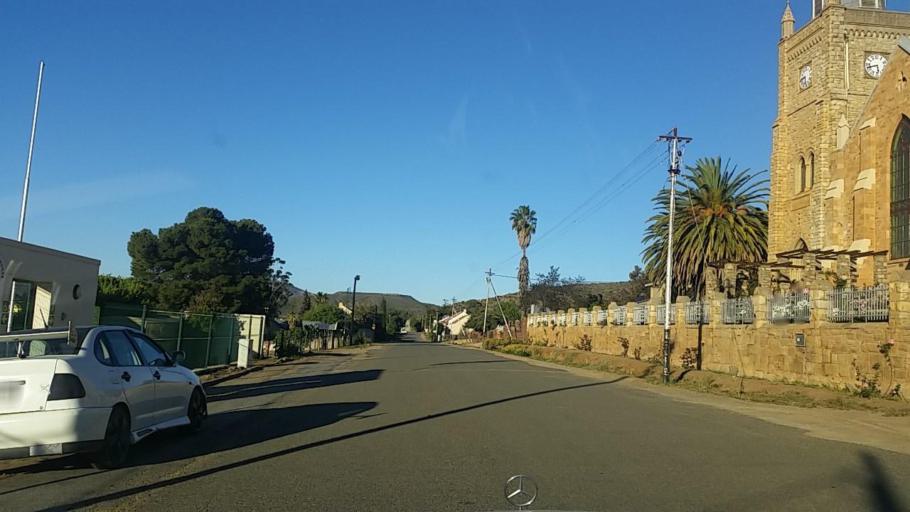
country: ZA
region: Western Cape
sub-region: Eden District Municipality
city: Knysna
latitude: -33.6581
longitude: 23.1263
